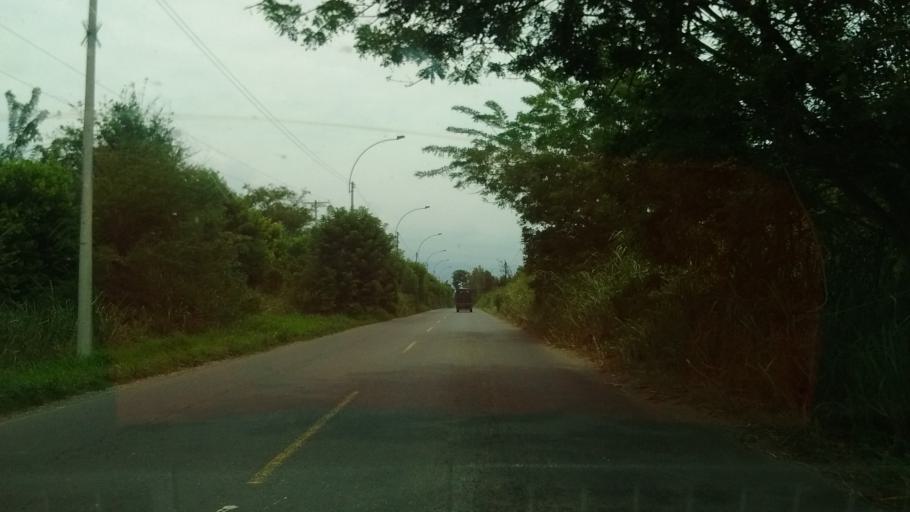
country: CO
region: Valle del Cauca
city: Jamundi
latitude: 3.3314
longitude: -76.5093
